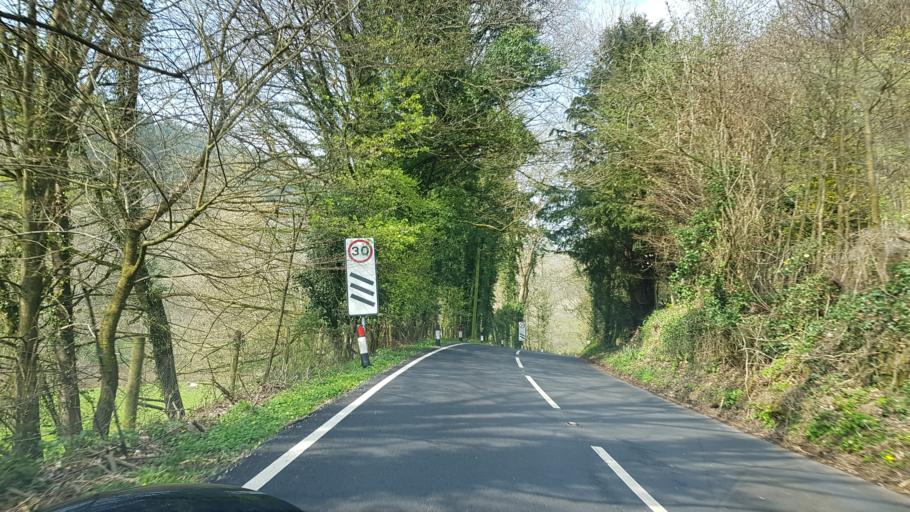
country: GB
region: Wales
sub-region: Monmouthshire
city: Monmouth
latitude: 51.7805
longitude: -2.6750
